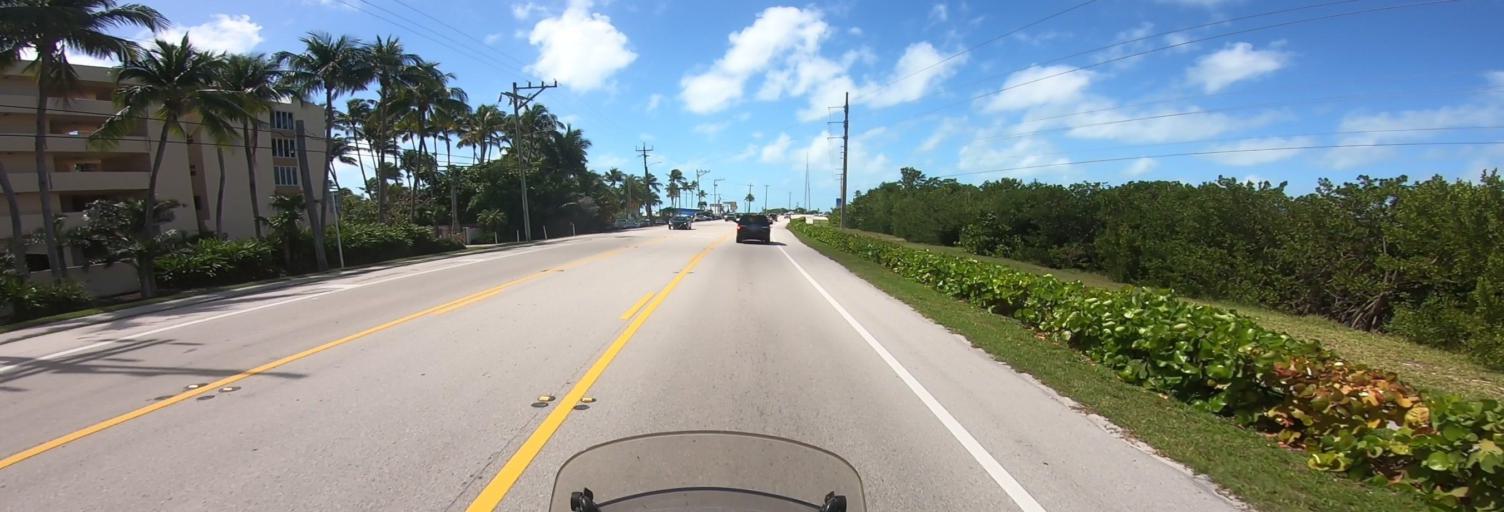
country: US
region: Florida
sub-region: Monroe County
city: Islamorada
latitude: 24.8994
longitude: -80.6570
